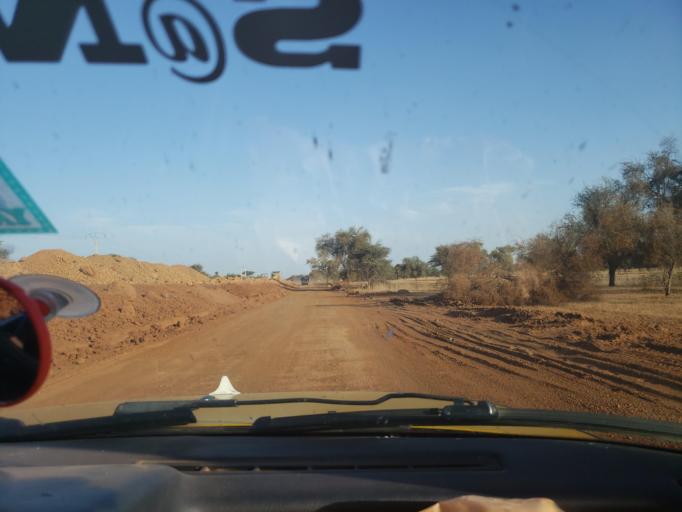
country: SN
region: Louga
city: Dara
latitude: 15.4146
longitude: -15.7081
